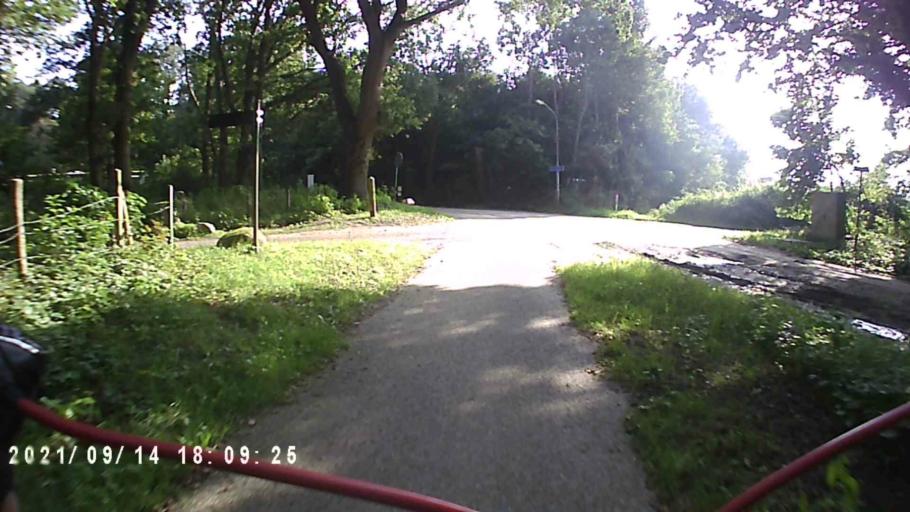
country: NL
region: Drenthe
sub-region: Gemeente Tynaarlo
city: Zuidlaren
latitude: 53.0986
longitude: 6.6552
